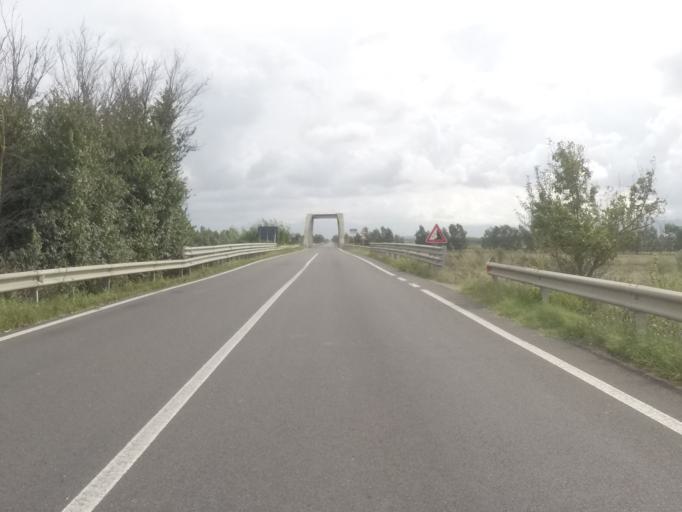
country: IT
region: Sardinia
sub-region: Provincia di Oristano
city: San Nicolo d'Arcidano
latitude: 39.6765
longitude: 8.6513
